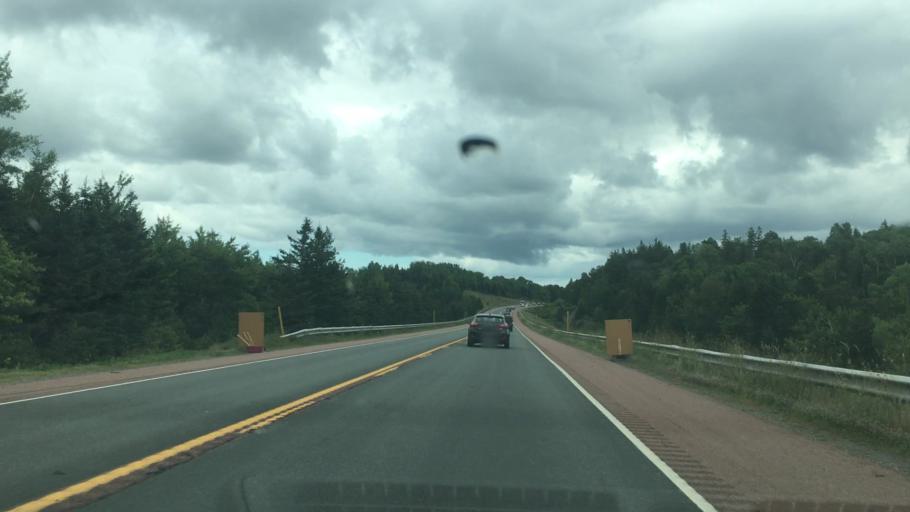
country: CA
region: Nova Scotia
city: Antigonish
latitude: 45.5937
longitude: -62.0616
